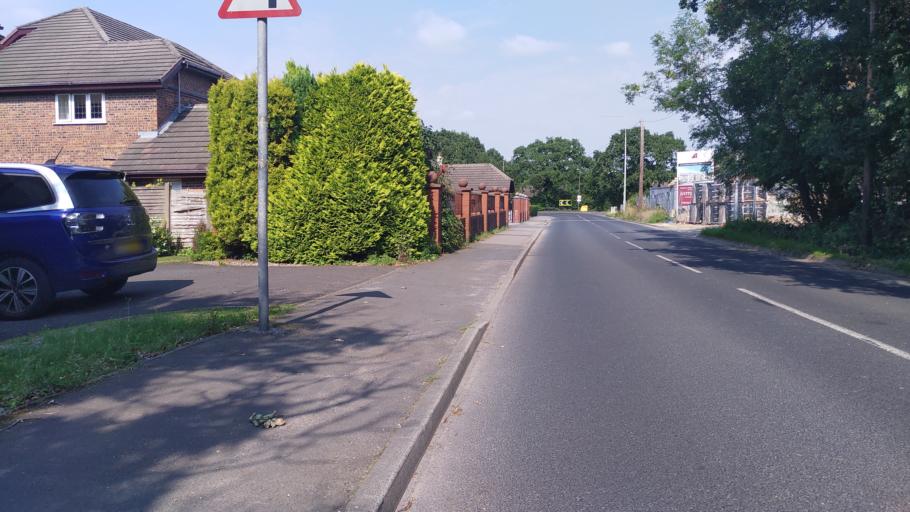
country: GB
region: England
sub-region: Lancashire
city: Clayton-le-Woods
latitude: 53.7216
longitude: -2.6359
